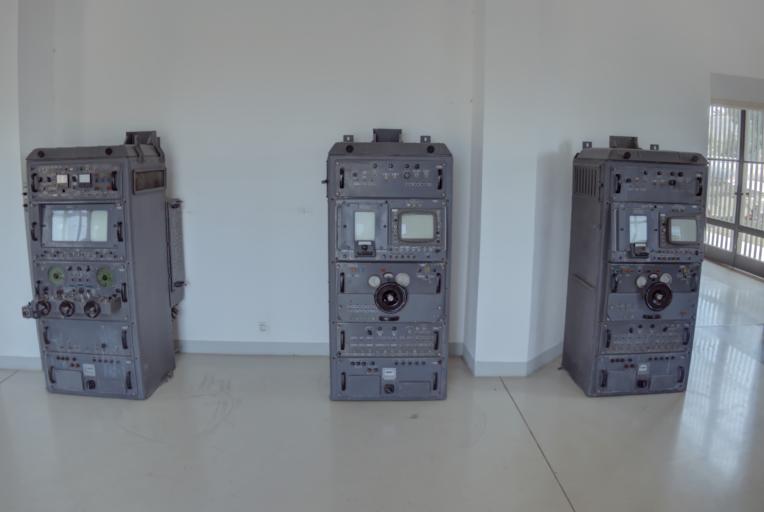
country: HU
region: Jasz-Nagykun-Szolnok
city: Szolnok
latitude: 47.1672
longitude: 20.1786
